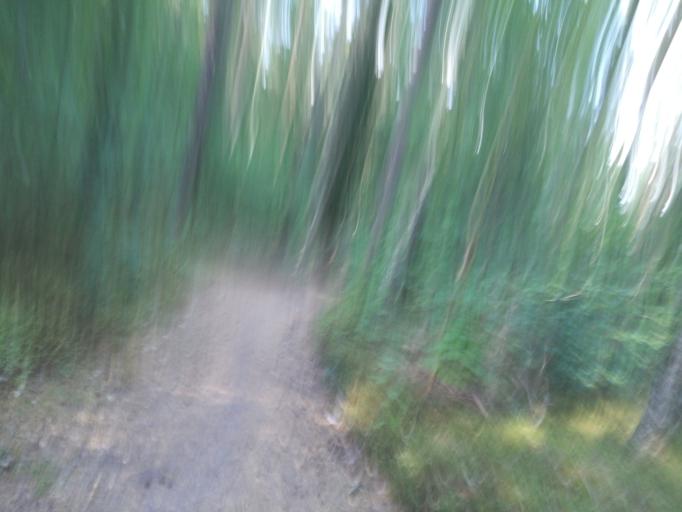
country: DE
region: Bavaria
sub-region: Regierungsbezirk Mittelfranken
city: Zirndorf
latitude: 49.4710
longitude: 10.9292
